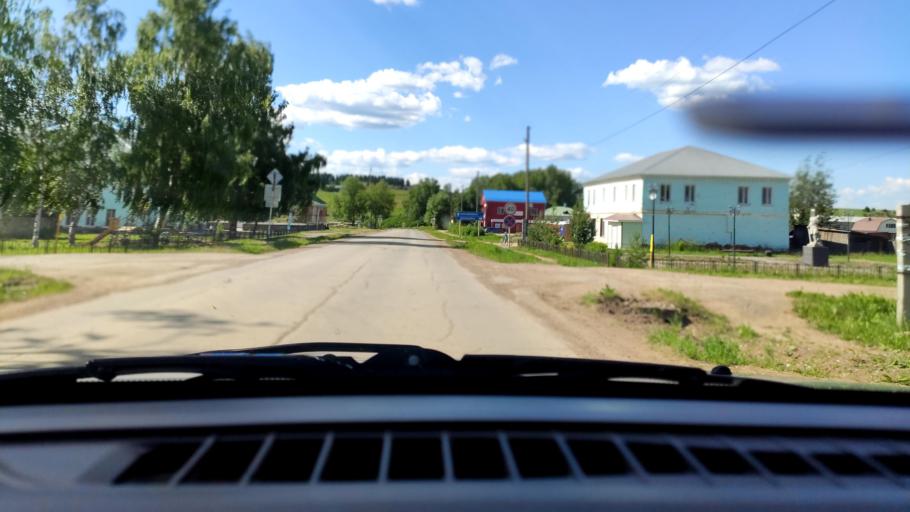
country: RU
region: Perm
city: Uinskoye
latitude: 57.1163
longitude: 56.5263
